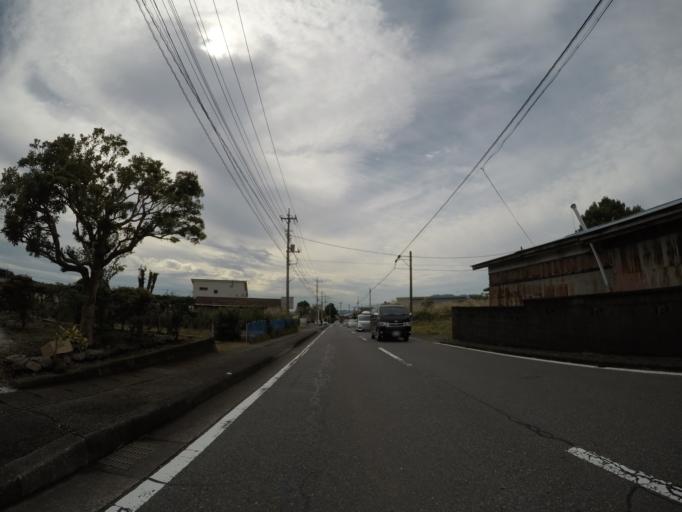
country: JP
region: Shizuoka
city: Fuji
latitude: 35.2190
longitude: 138.6884
